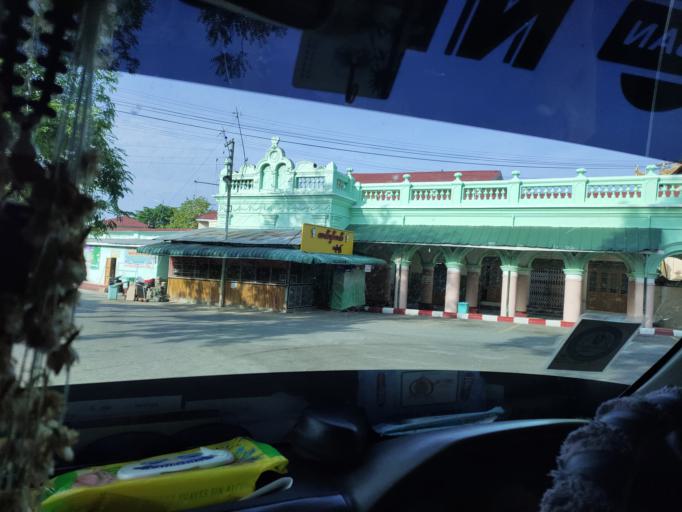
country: MM
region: Magway
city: Magway
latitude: 20.1696
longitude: 94.9185
